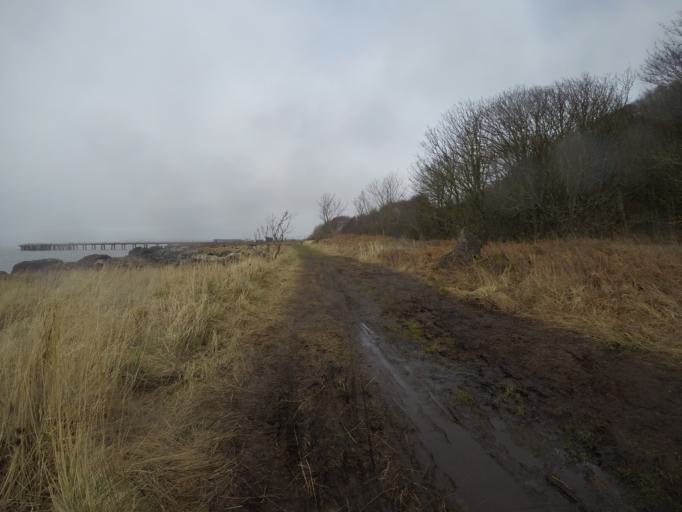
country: GB
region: Scotland
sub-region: North Ayrshire
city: Millport
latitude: 55.7130
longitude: -4.9033
